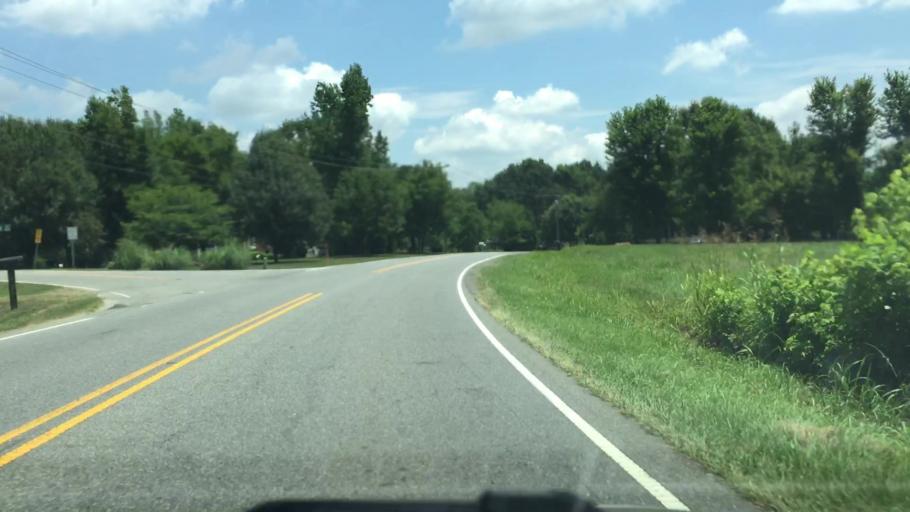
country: US
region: North Carolina
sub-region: Cabarrus County
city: Kannapolis
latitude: 35.4266
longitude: -80.7122
